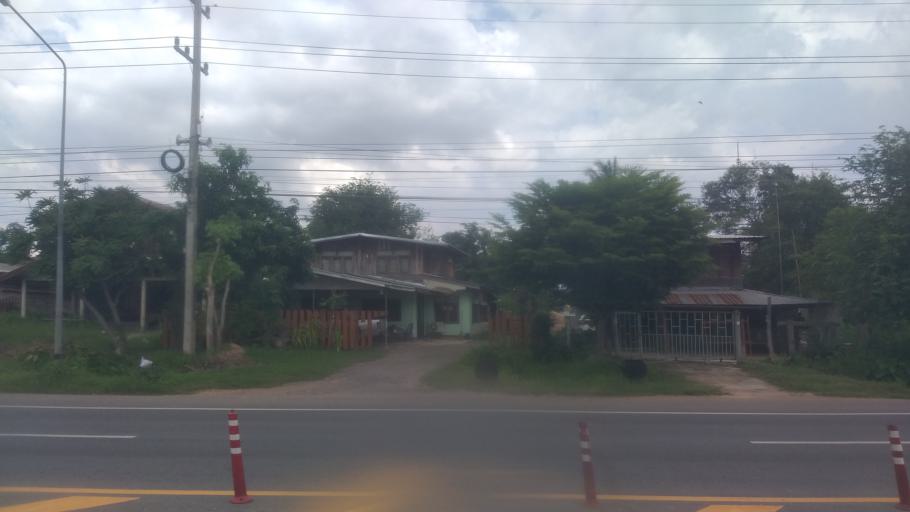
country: TH
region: Chaiyaphum
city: Noen Sa-nga
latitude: 15.6722
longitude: 101.9625
